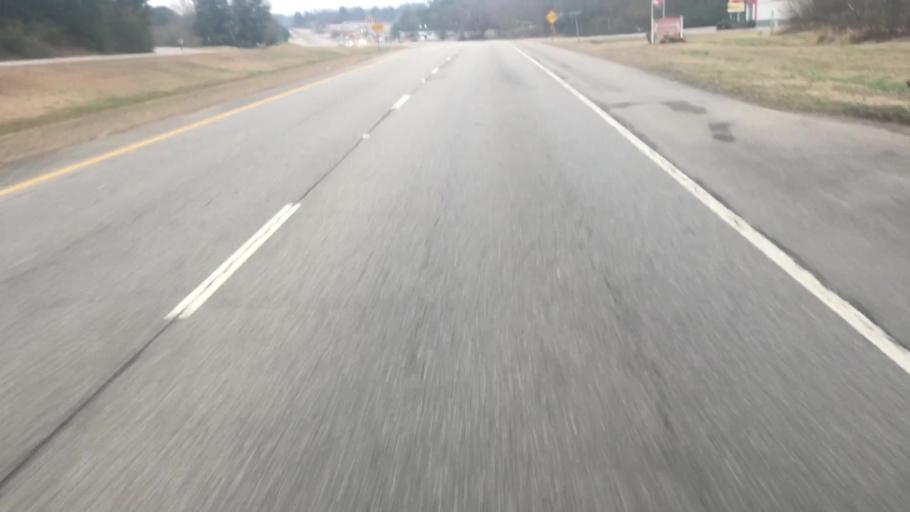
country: US
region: Alabama
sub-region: Walker County
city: Sumiton
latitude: 33.7646
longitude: -87.0695
